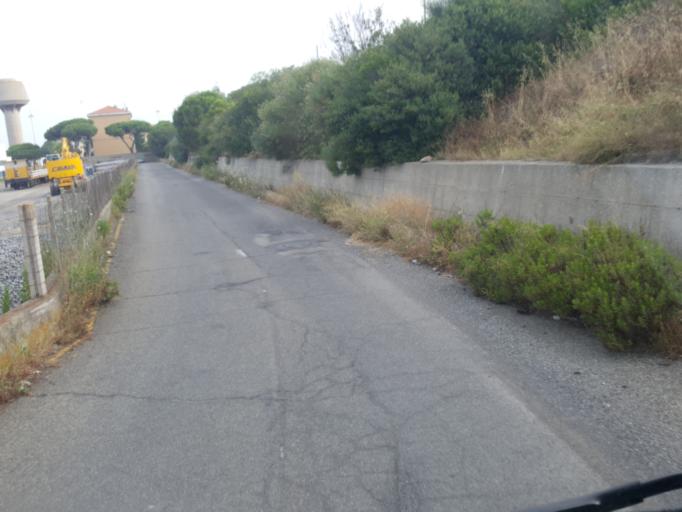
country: IT
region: Latium
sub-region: Citta metropolitana di Roma Capitale
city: Civitavecchia
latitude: 42.1000
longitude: 11.7897
